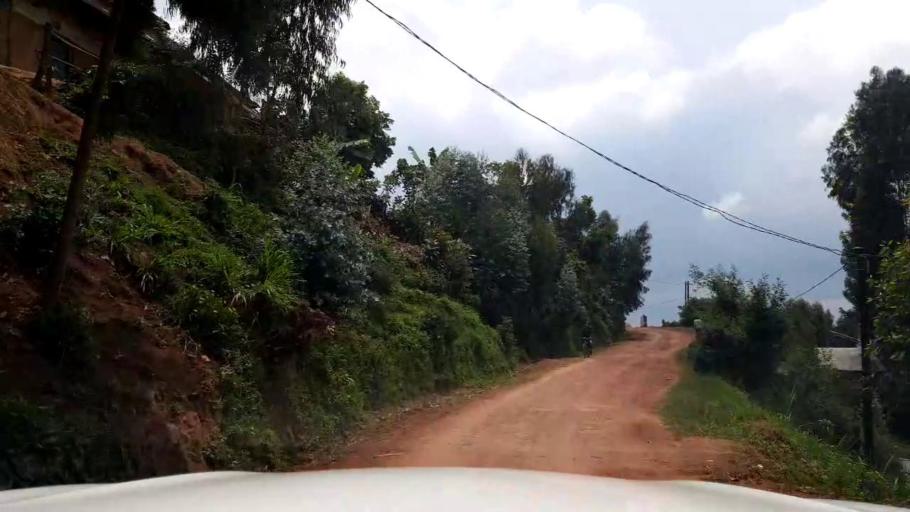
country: RW
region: Northern Province
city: Byumba
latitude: -1.4911
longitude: 29.9296
